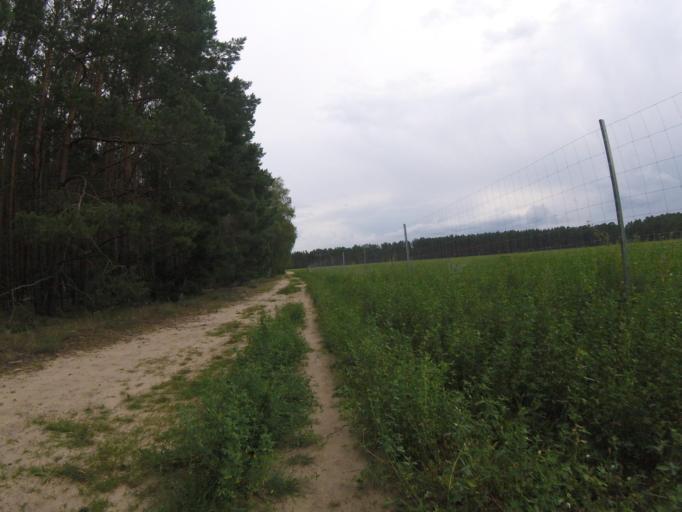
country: DE
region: Brandenburg
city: Bestensee
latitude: 52.2200
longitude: 13.6636
